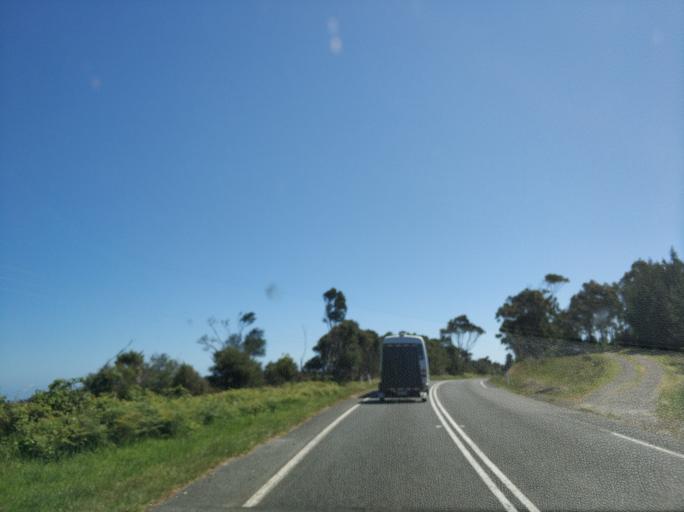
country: AU
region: Victoria
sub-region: Colac-Otway
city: Apollo Bay
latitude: -38.7359
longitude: 143.3030
